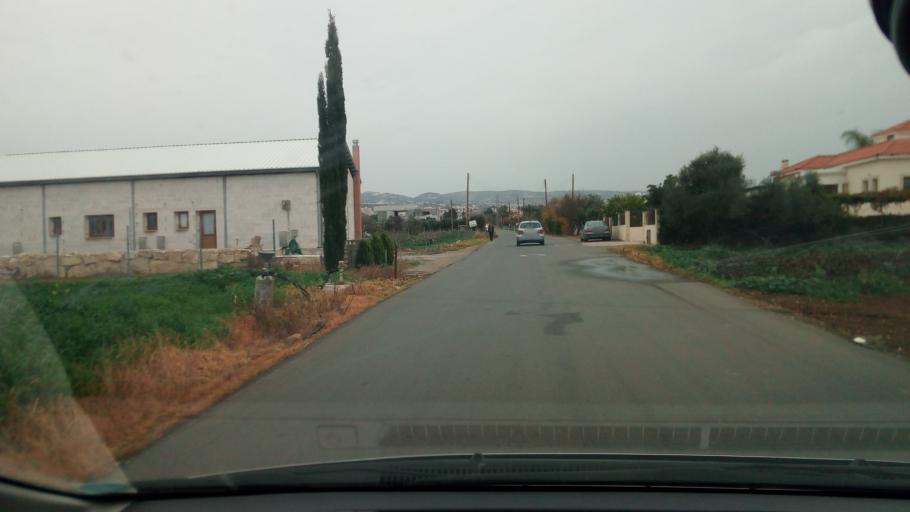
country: CY
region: Pafos
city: Chlorakas
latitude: 34.8051
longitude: 32.4124
